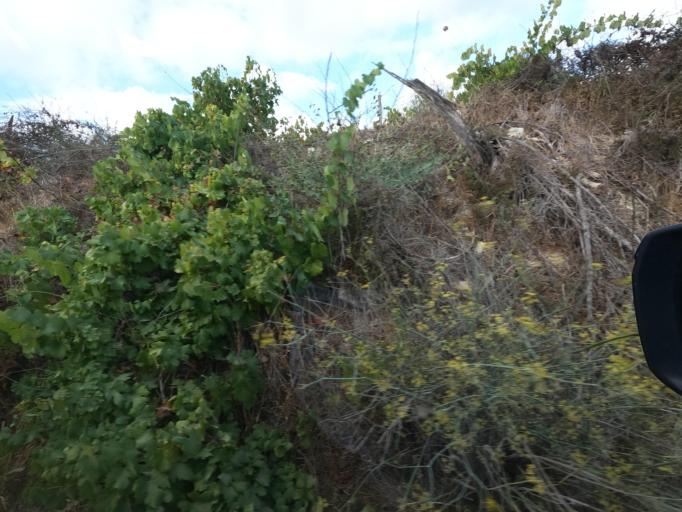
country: CY
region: Pafos
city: Mesogi
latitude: 34.8482
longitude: 32.5379
